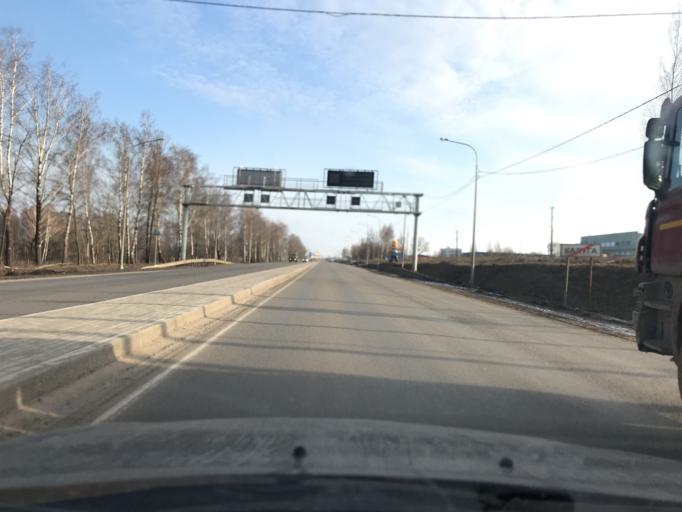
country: RU
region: Kaluga
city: Kaluga
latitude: 54.4892
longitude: 36.2293
